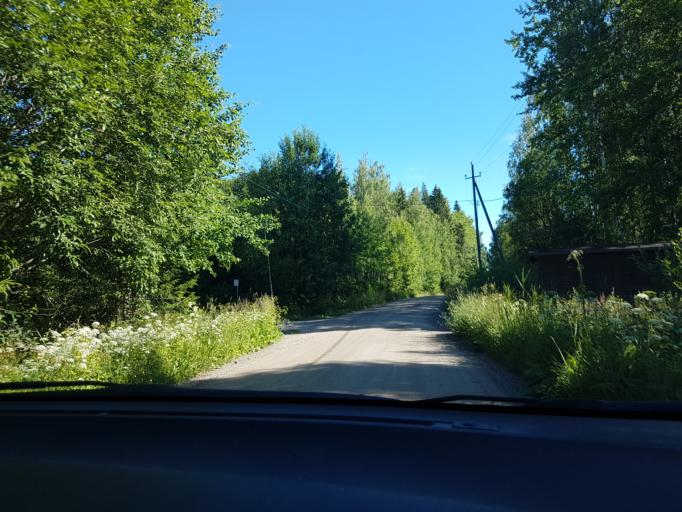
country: FI
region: Uusimaa
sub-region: Helsinki
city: Sibbo
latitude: 60.2833
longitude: 25.2389
